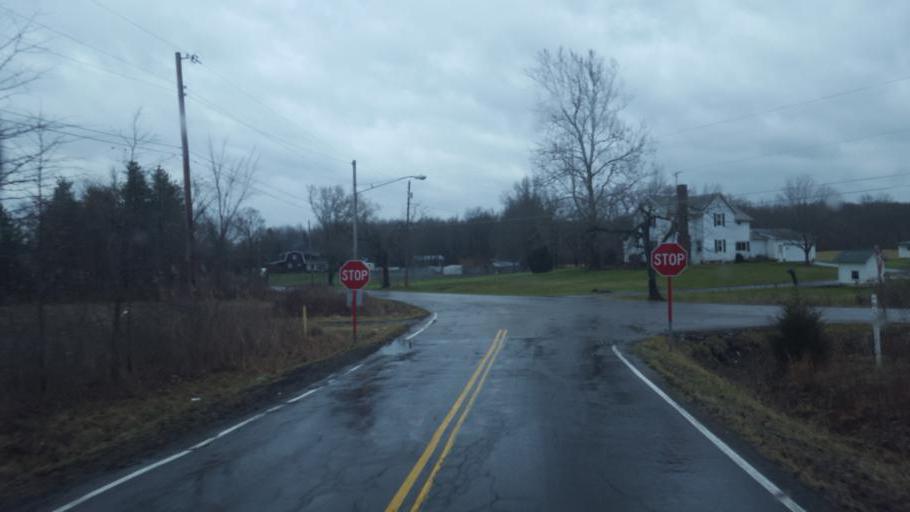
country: US
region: Ohio
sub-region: Portage County
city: Garrettsville
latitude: 41.3556
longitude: -80.9738
